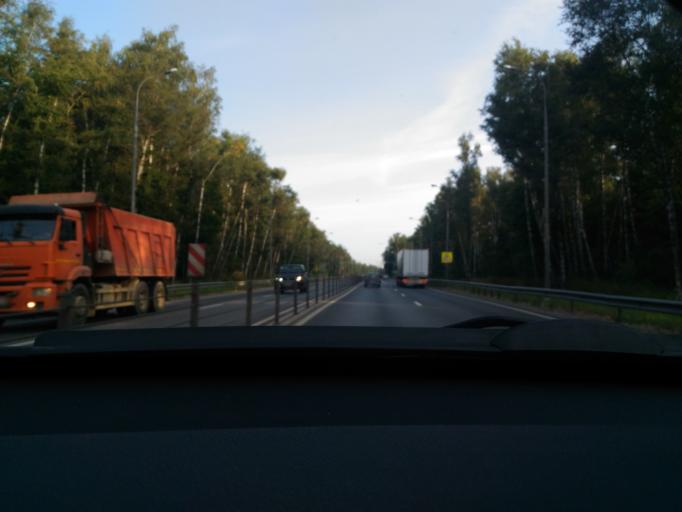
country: RU
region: Moskovskaya
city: Marfino
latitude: 56.0218
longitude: 37.5445
